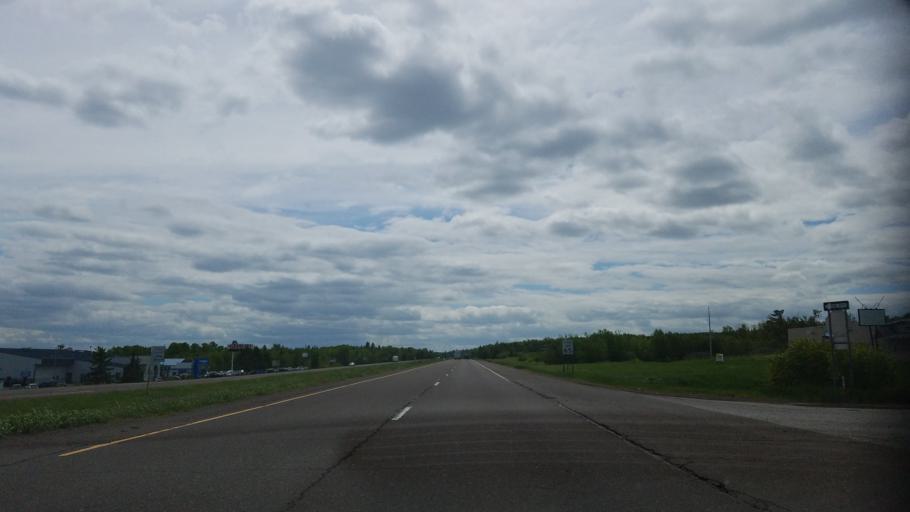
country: US
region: Minnesota
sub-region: Lake County
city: Two Harbors
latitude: 47.0117
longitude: -91.7096
